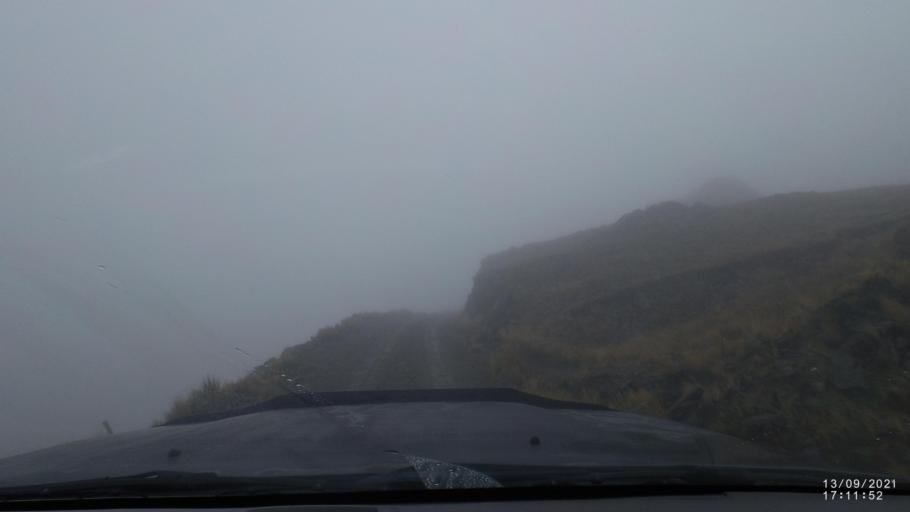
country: BO
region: Cochabamba
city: Colomi
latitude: -17.3376
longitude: -65.7443
